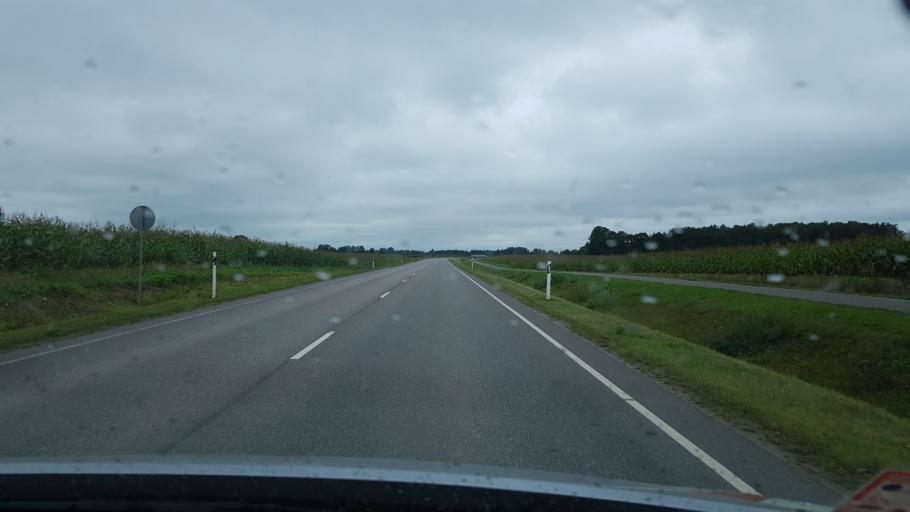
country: EE
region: Viljandimaa
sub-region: Vohma linn
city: Vohma
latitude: 58.6324
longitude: 25.7199
